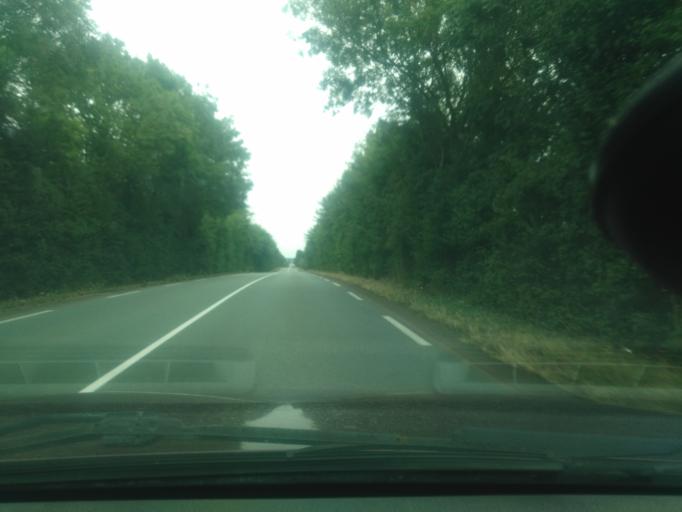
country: FR
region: Pays de la Loire
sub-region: Departement de la Vendee
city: Chantonnay
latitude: 46.6832
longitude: -1.0194
